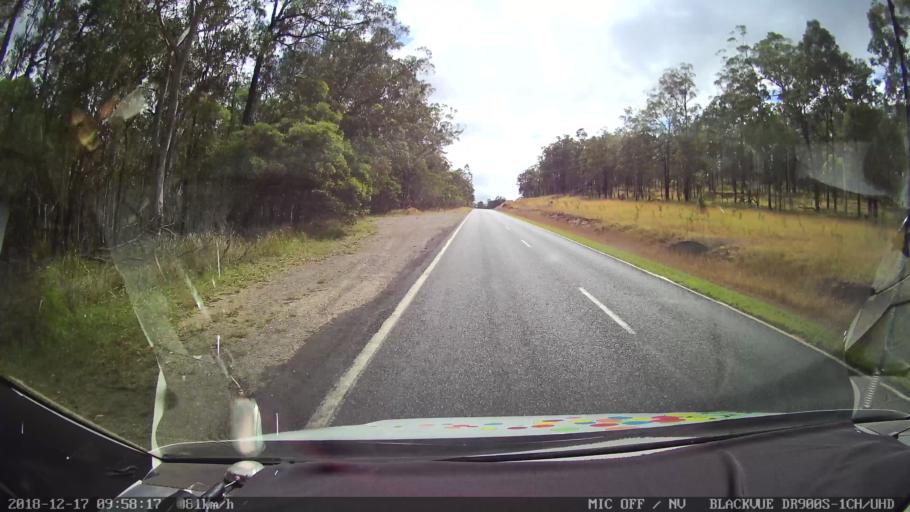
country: AU
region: New South Wales
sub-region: Tenterfield Municipality
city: Carrolls Creek
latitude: -28.9200
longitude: 152.4071
